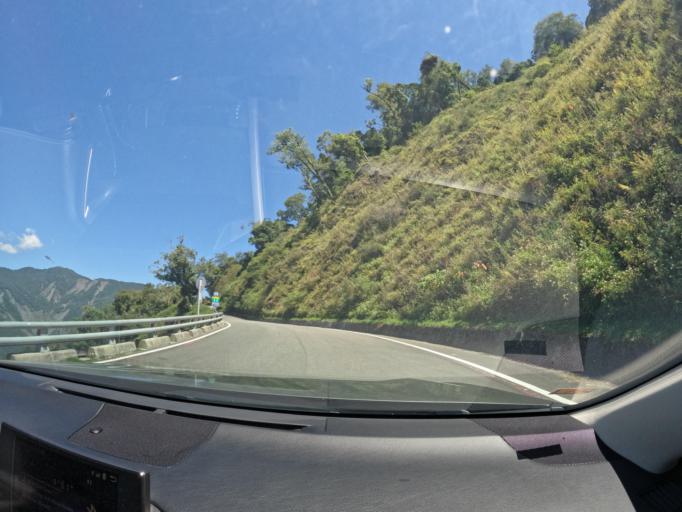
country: TW
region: Taiwan
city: Yujing
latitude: 23.2854
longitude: 120.8962
